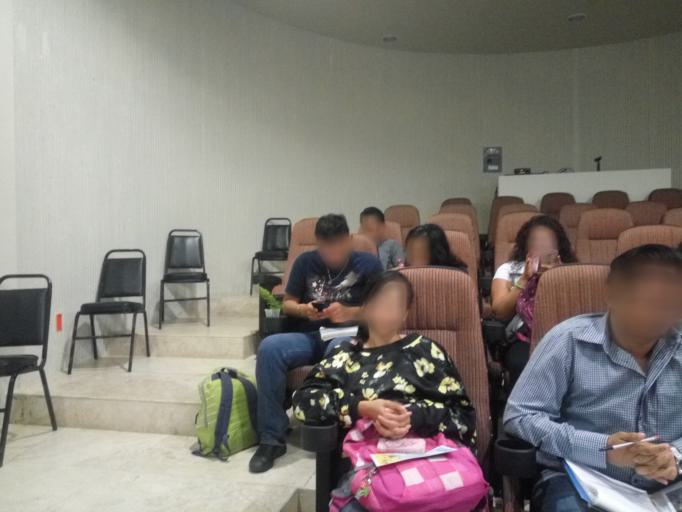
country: MX
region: Tabasco
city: Villahermosa
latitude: 17.9788
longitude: -92.9234
